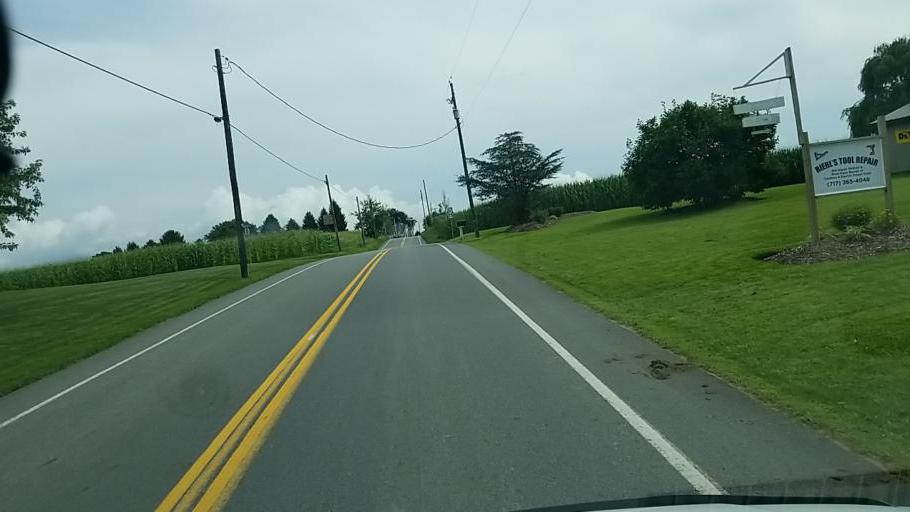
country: US
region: Pennsylvania
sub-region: Dauphin County
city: Elizabethville
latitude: 40.6093
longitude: -76.7797
